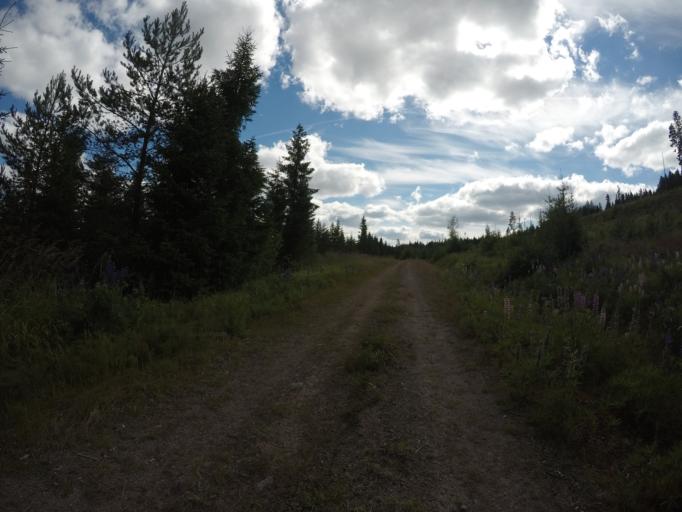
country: SE
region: Vaermland
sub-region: Filipstads Kommun
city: Lesjofors
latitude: 60.0809
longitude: 14.4598
